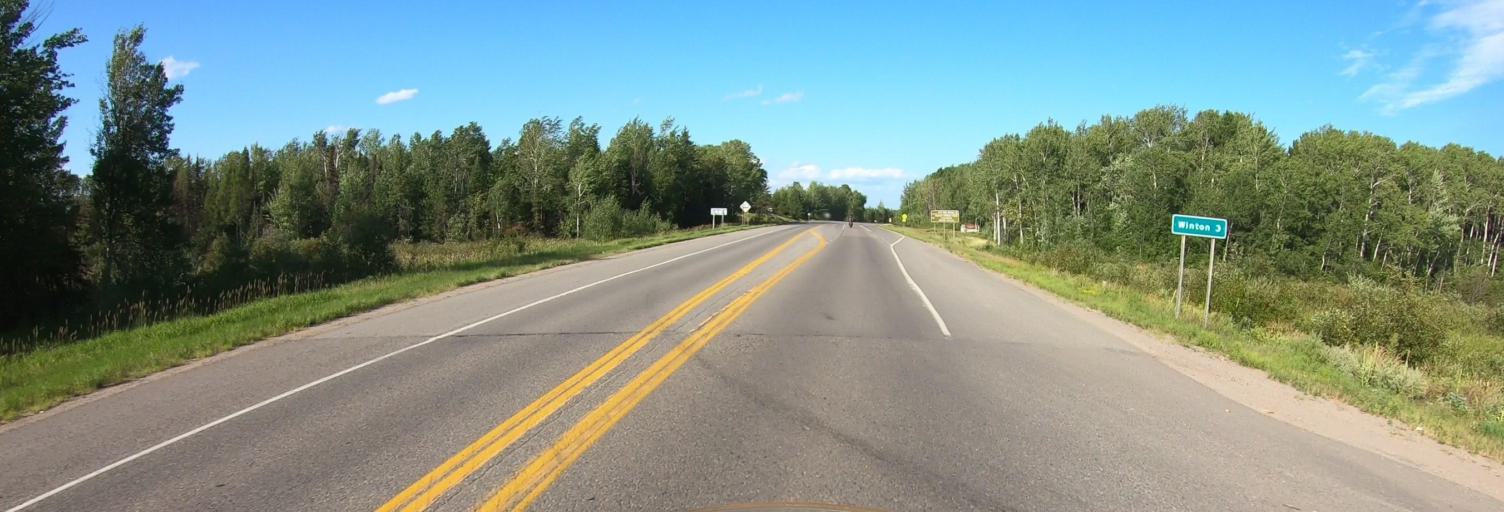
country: US
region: Minnesota
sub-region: Saint Louis County
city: Ely
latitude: 47.9045
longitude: -91.8314
